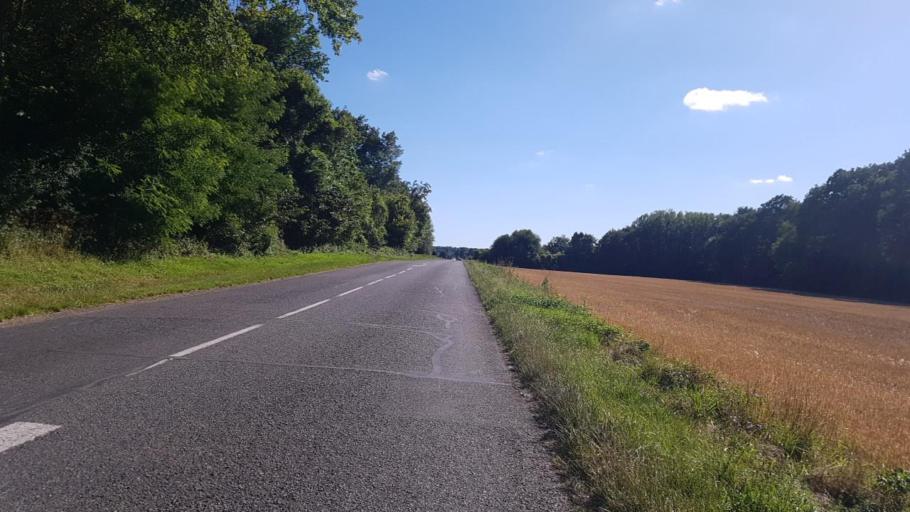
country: FR
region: Ile-de-France
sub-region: Departement de Seine-et-Marne
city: Esbly
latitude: 48.9177
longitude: 2.7907
